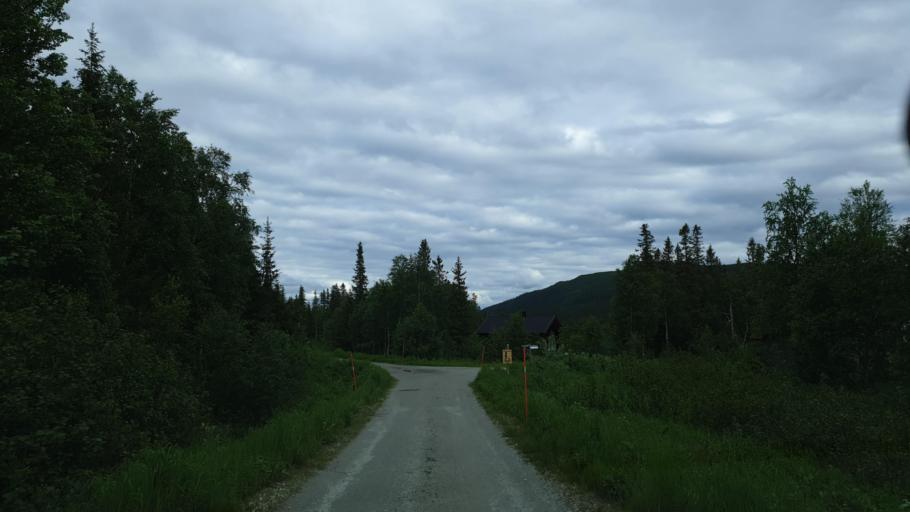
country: SE
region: Vaesterbotten
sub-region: Vilhelmina Kommun
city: Sjoberg
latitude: 65.2515
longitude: 15.5150
